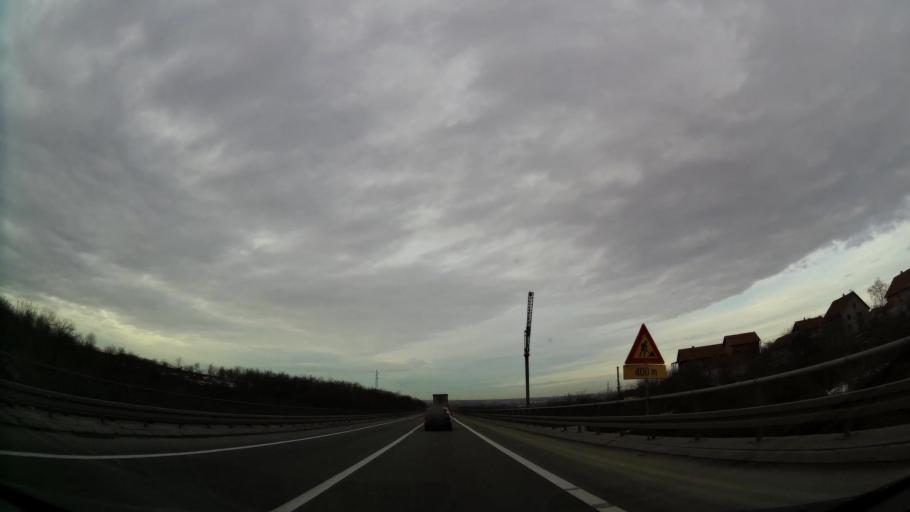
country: RS
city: Ostruznica
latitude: 44.7181
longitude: 20.3603
